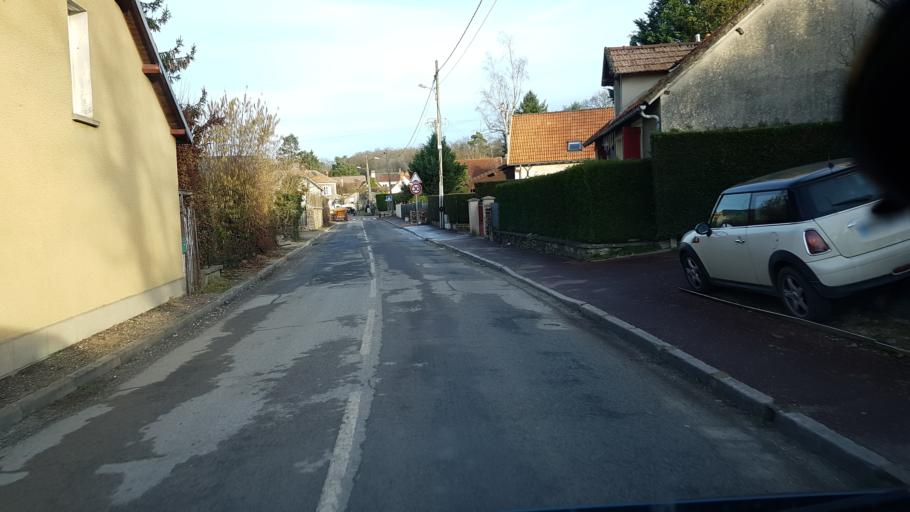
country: FR
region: Ile-de-France
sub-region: Departement des Yvelines
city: Gazeran
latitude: 48.6726
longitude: 1.7474
